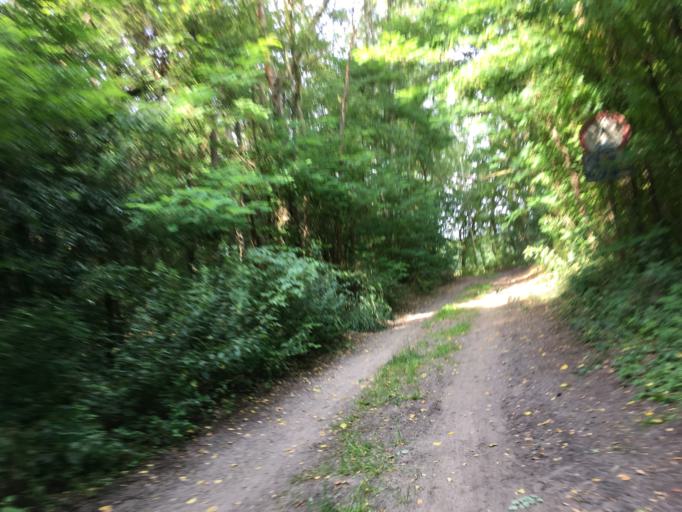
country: DE
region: Brandenburg
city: Rudnitz
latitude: 52.7382
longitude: 13.5809
